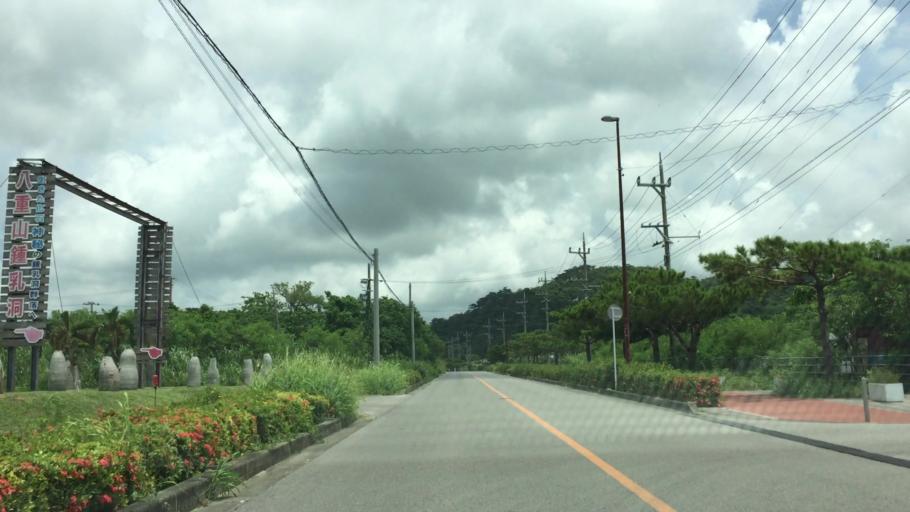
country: JP
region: Okinawa
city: Ishigaki
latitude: 24.3629
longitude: 124.1569
